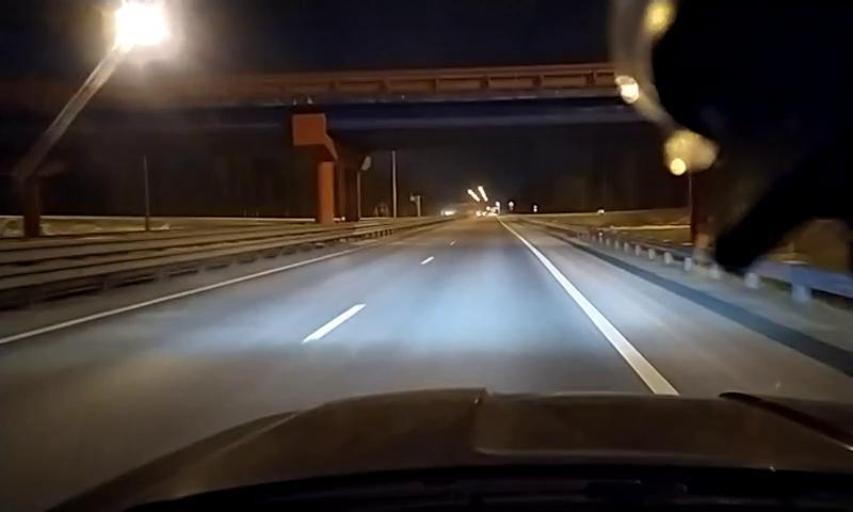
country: RU
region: Leningrad
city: Agalatovo
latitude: 60.2223
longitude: 30.3586
